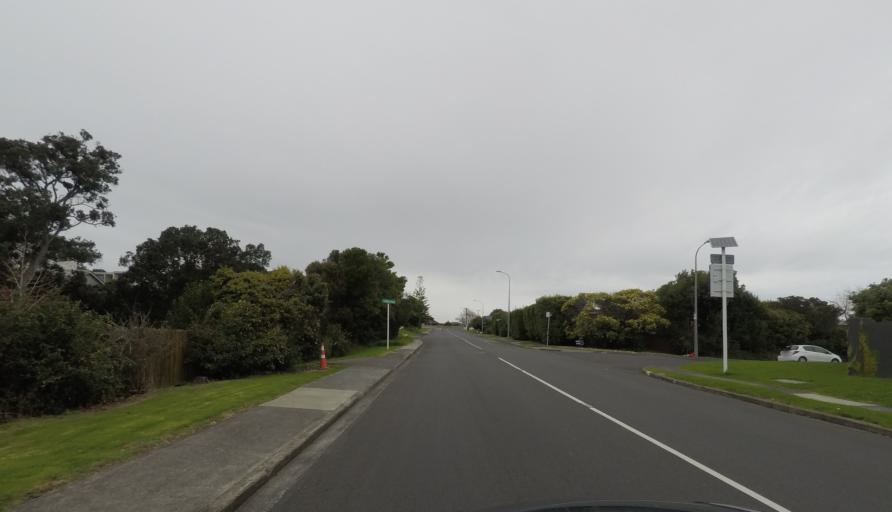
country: NZ
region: Auckland
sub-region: Auckland
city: Pakuranga
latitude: -36.8953
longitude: 174.9435
